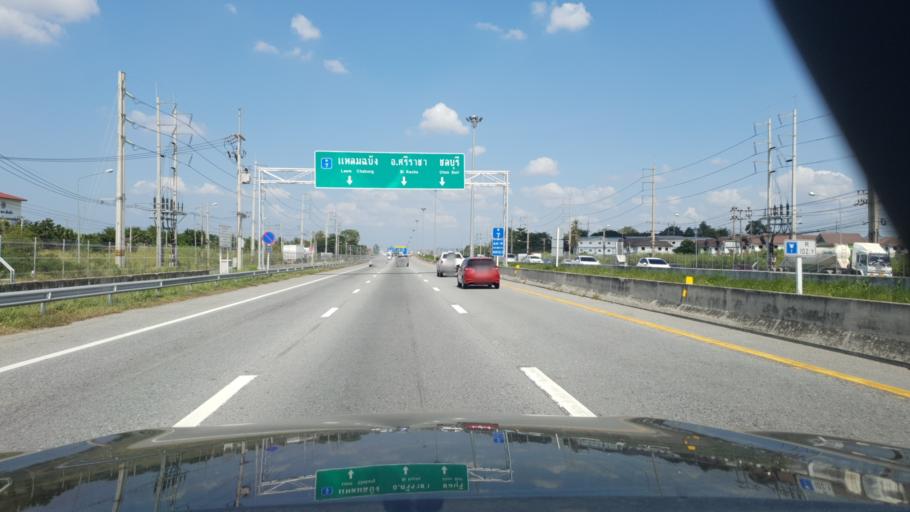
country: TH
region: Chon Buri
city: Ban Talat Bueng
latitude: 13.0923
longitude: 100.9903
